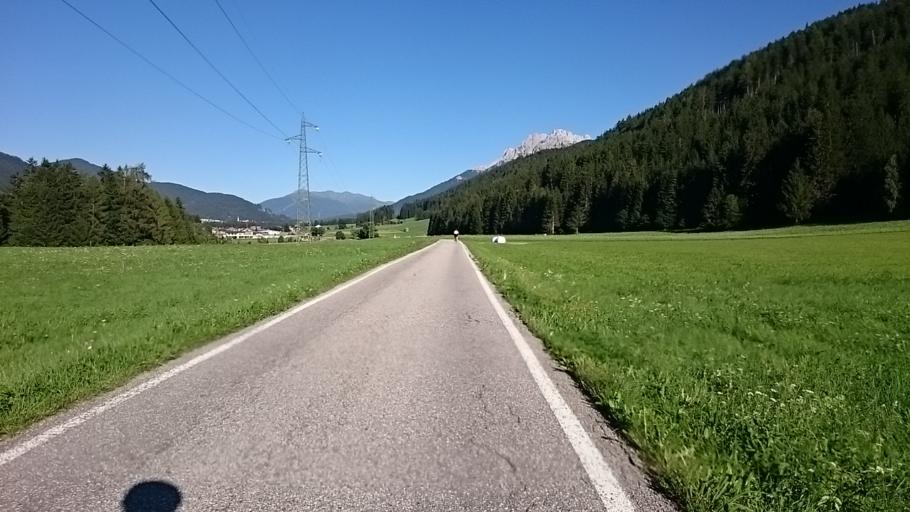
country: IT
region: Trentino-Alto Adige
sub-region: Bolzano
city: Braies
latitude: 46.7382
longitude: 12.1485
